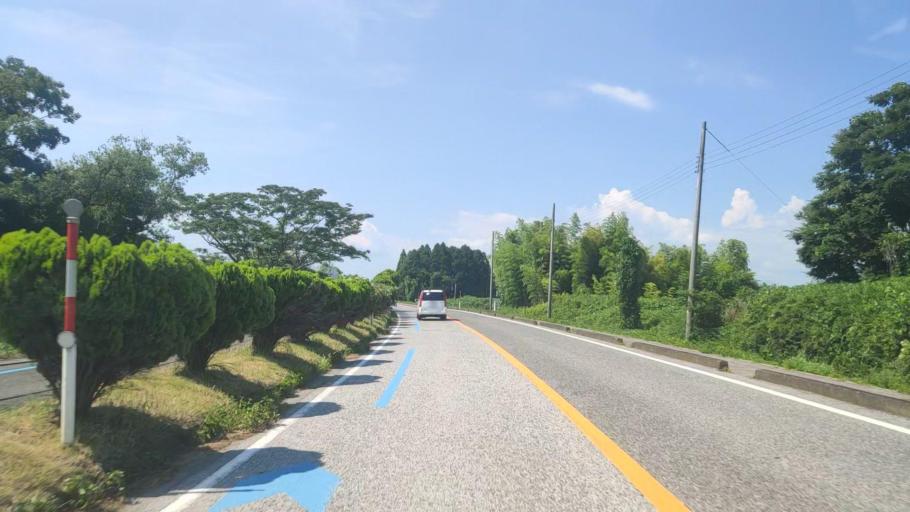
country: JP
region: Shiga Prefecture
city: Nagahama
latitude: 35.3973
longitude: 136.2179
